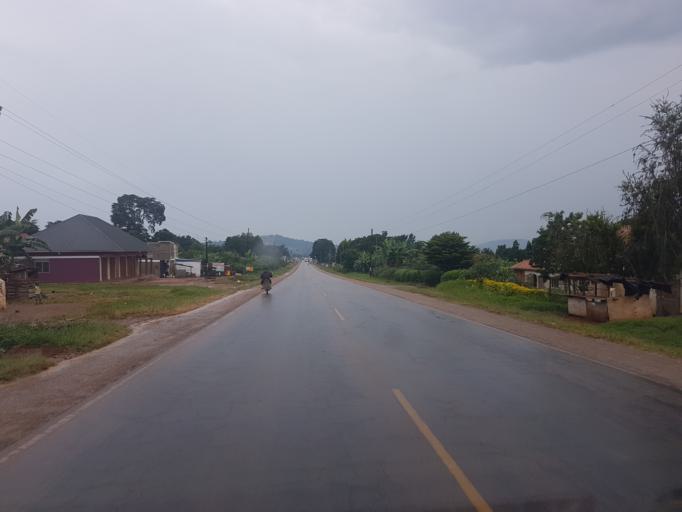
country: UG
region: Central Region
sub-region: Butambala District
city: Gombe
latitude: 0.0685
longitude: 32.1140
